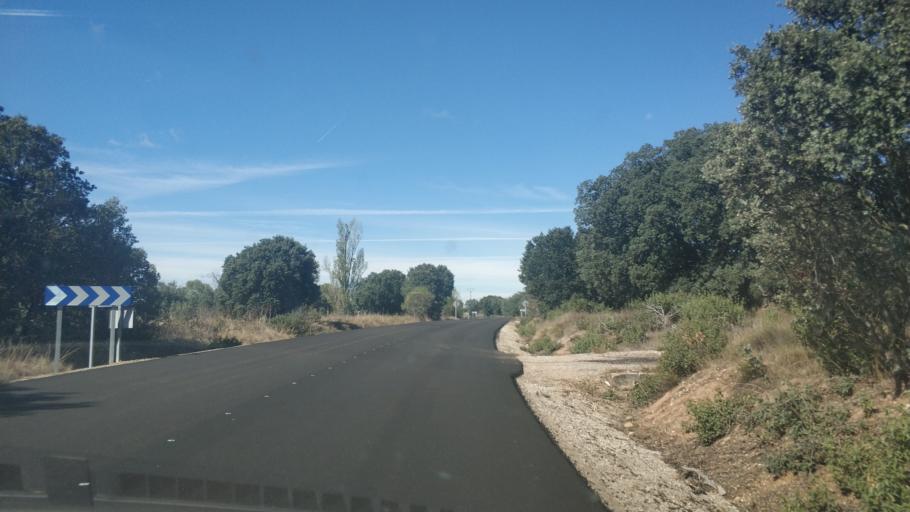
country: ES
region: Castille and Leon
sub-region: Provincia de Burgos
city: Puentedura
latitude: 42.0332
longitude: -3.6188
